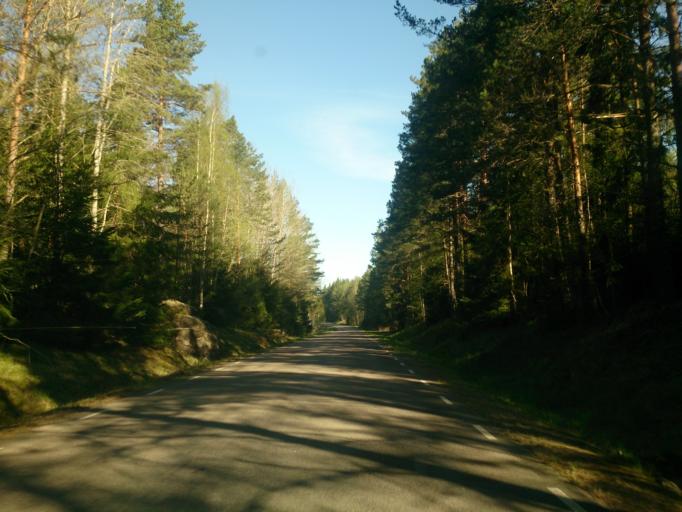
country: SE
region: OEstergoetland
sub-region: Linkopings Kommun
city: Ljungsbro
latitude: 58.6176
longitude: 15.4693
